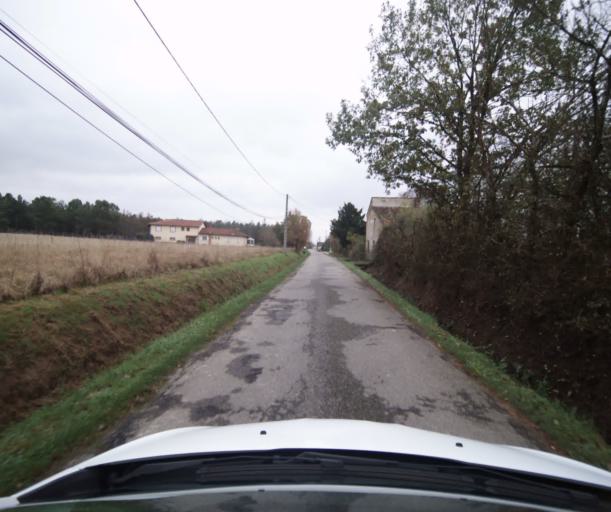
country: FR
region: Midi-Pyrenees
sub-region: Departement du Tarn-et-Garonne
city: Castelsarrasin
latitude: 44.0597
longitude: 1.1455
